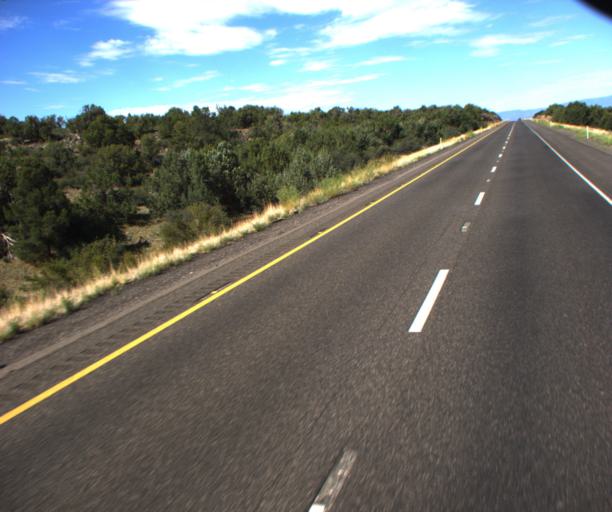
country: US
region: Arizona
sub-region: Yavapai County
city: Village of Oak Creek (Big Park)
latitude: 34.7794
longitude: -111.6250
